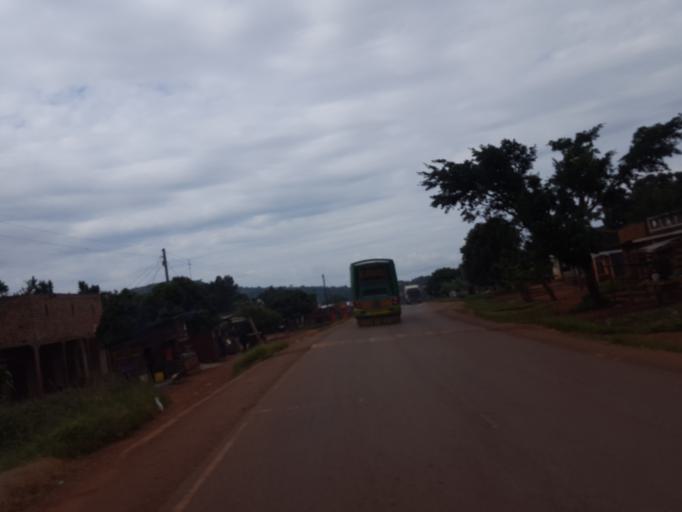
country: UG
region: Central Region
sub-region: Mityana District
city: Mityana
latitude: 0.6627
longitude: 32.0907
